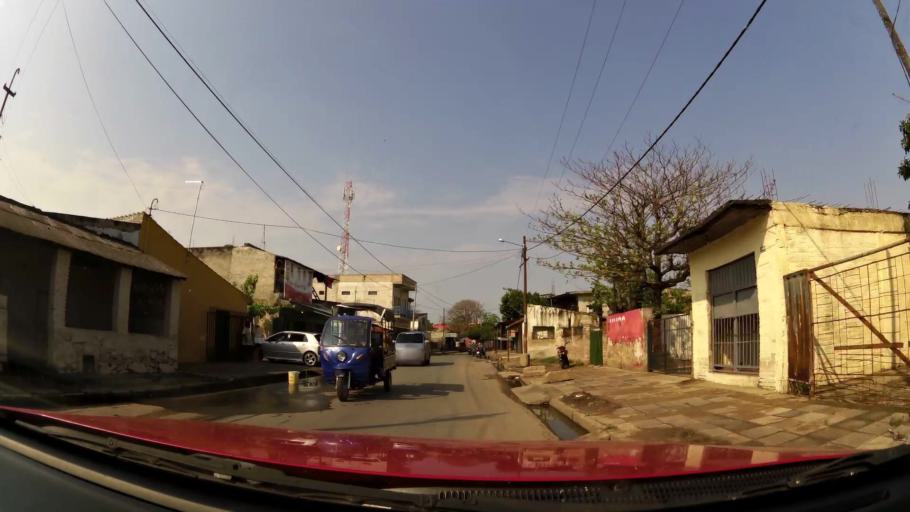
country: PY
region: Asuncion
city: Asuncion
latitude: -25.3027
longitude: -57.6659
